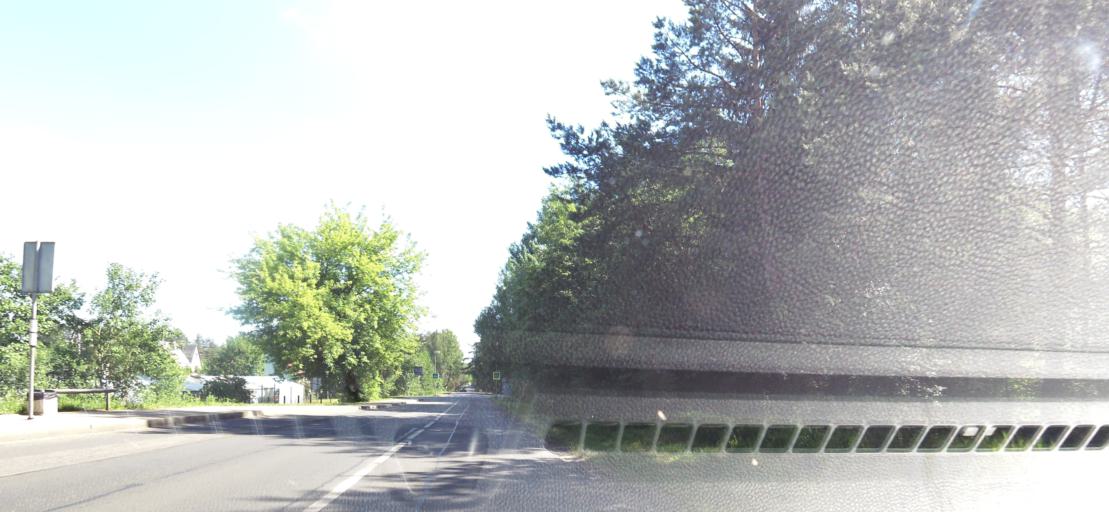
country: LT
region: Vilnius County
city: Rasos
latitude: 54.7961
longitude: 25.3498
